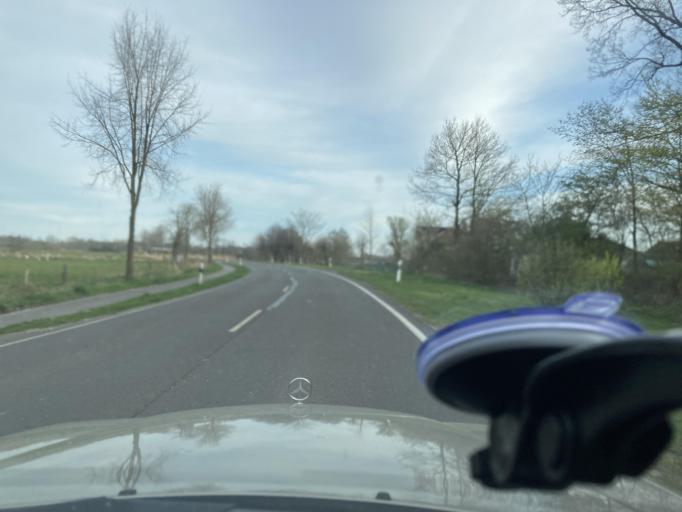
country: DE
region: Schleswig-Holstein
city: Stelle-Wittenwurth
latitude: 54.2627
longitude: 9.0523
